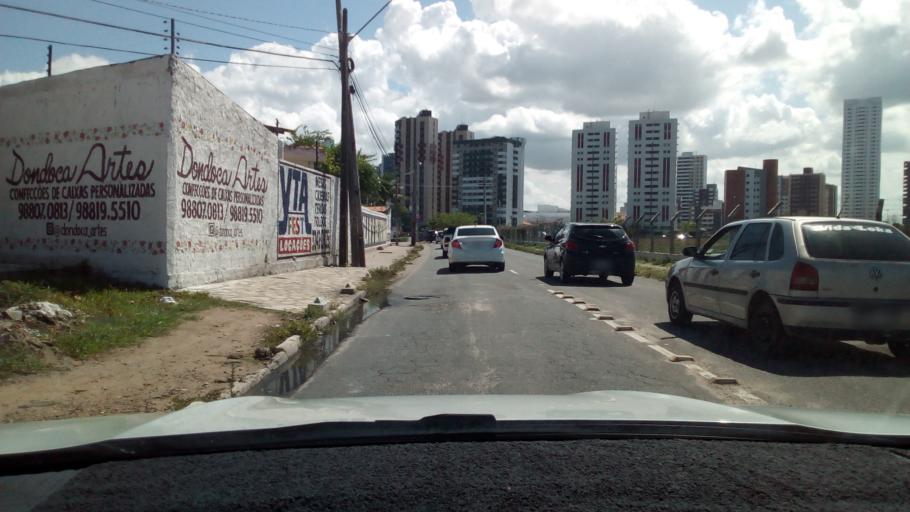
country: BR
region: Paraiba
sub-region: Joao Pessoa
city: Joao Pessoa
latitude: -7.0947
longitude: -34.8376
